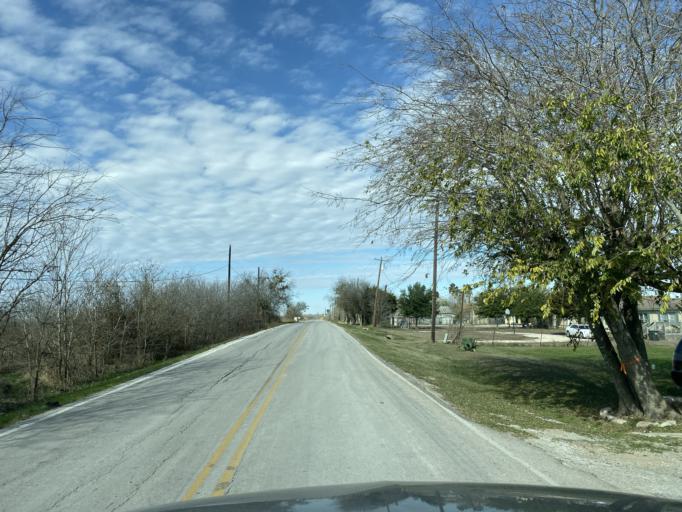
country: US
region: Texas
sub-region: Travis County
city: Onion Creek
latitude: 30.0842
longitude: -97.7029
